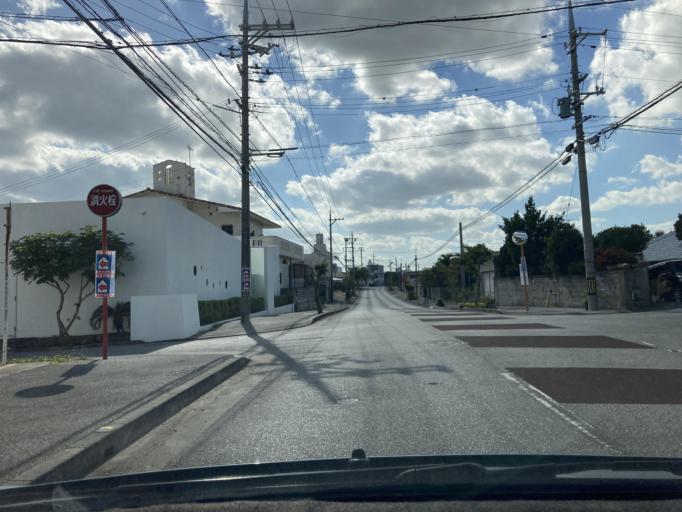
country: JP
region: Okinawa
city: Gushikawa
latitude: 26.3436
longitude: 127.8483
